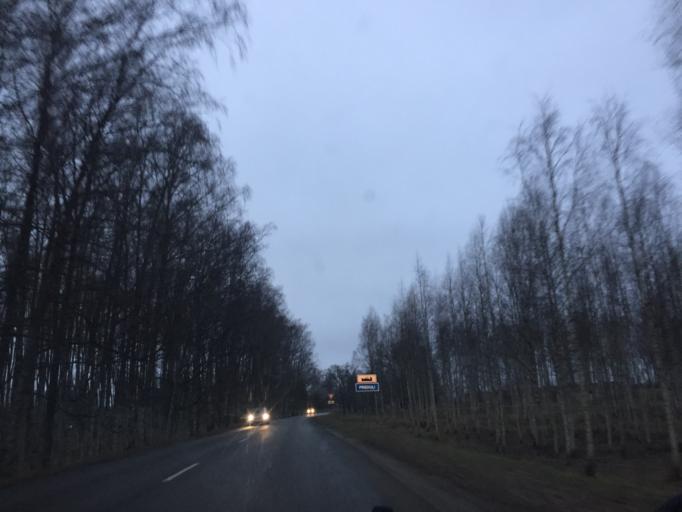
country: LV
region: Priekuli
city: Priekuli
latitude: 57.3177
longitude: 25.3699
